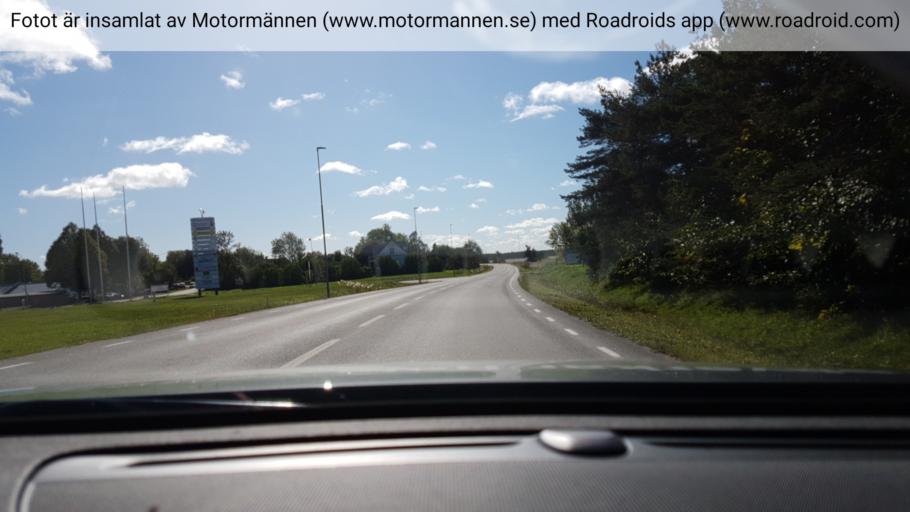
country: SE
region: Gotland
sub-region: Gotland
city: Slite
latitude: 57.7037
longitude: 18.7958
